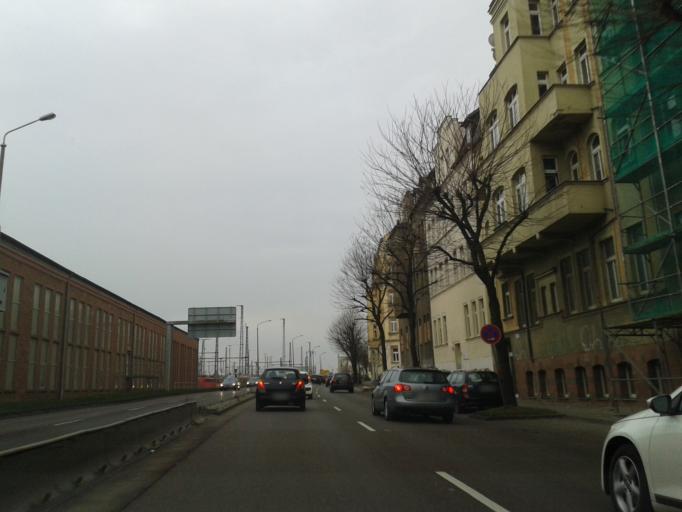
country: DE
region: Saxony-Anhalt
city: Halle (Saale)
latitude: 51.4871
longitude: 11.9846
